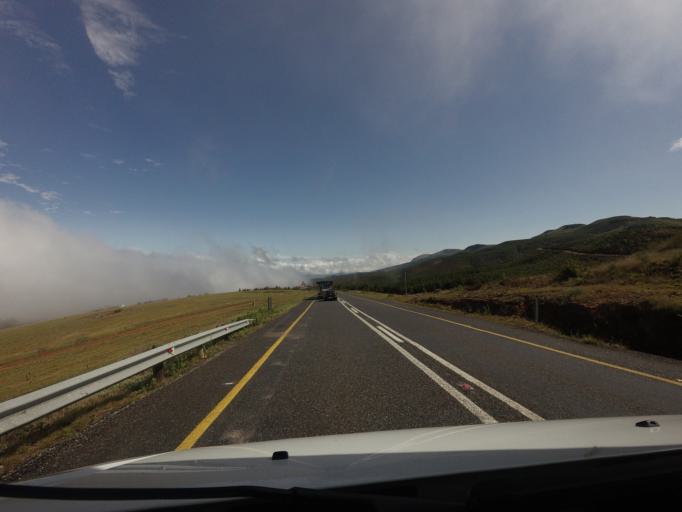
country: ZA
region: Mpumalanga
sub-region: Ehlanzeni District
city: Lydenburg
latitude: -25.1624
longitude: 30.6280
